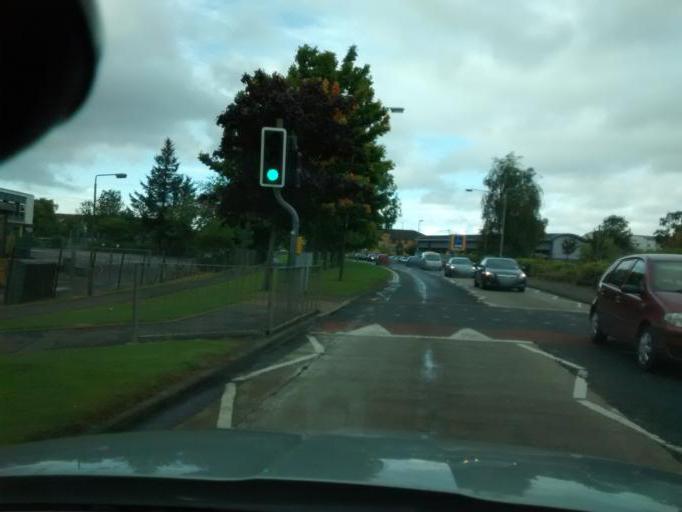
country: GB
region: Scotland
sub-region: West Lothian
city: Bathgate
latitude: 55.8996
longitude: -3.6460
